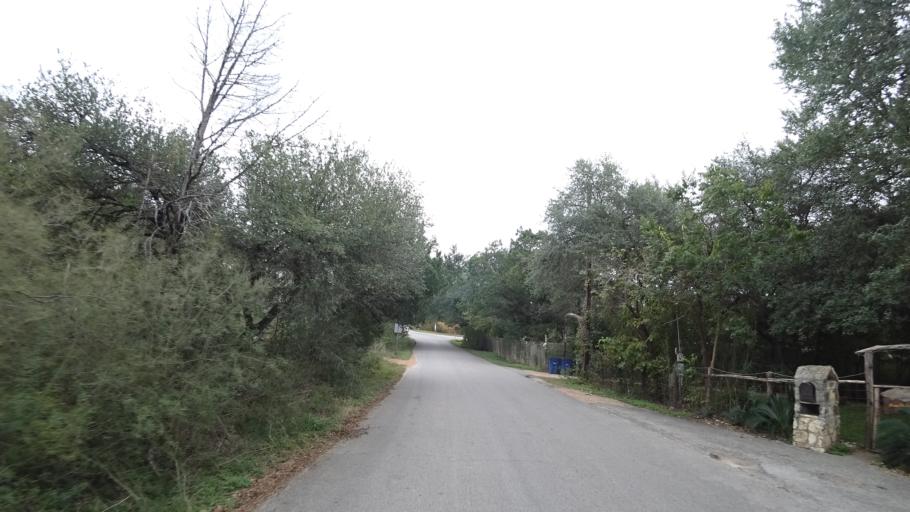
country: US
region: Texas
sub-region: Travis County
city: Bee Cave
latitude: 30.3295
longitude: -97.9271
